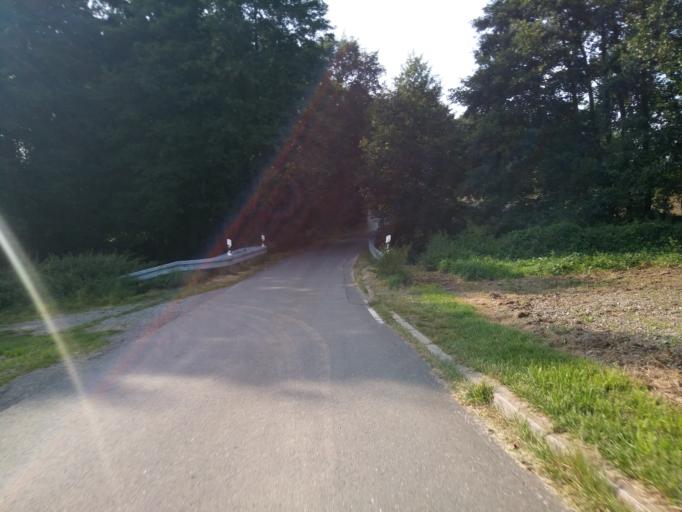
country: DE
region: Saxony
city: Syrau
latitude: 50.5624
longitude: 12.1189
